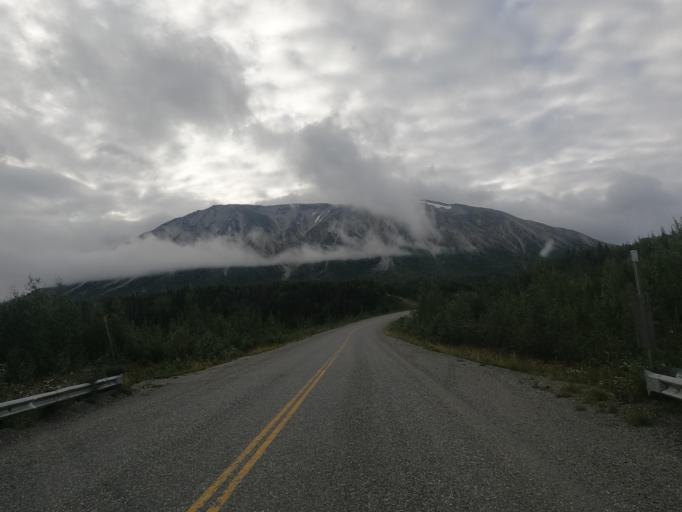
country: CA
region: Yukon
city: Haines Junction
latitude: 60.1113
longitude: -136.9282
